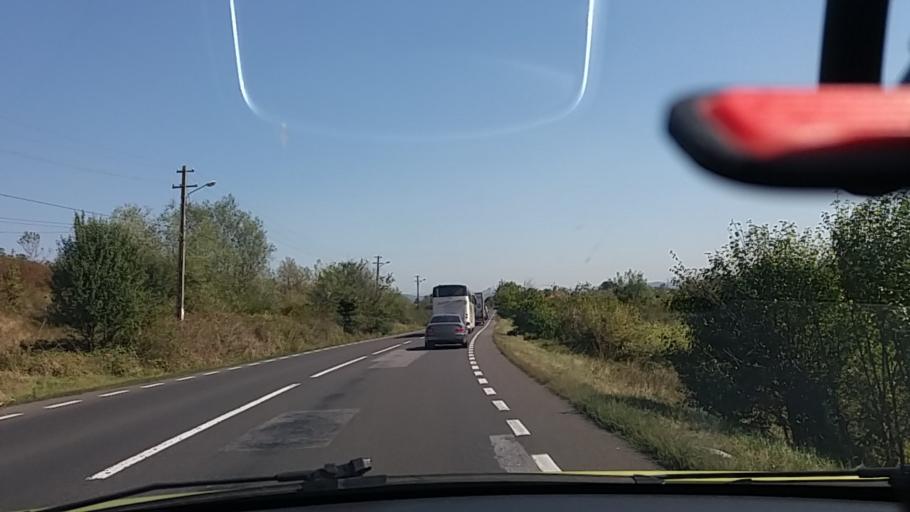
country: RO
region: Hunedoara
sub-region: Comuna Dobra
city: Dobra
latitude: 45.9497
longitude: 22.5817
